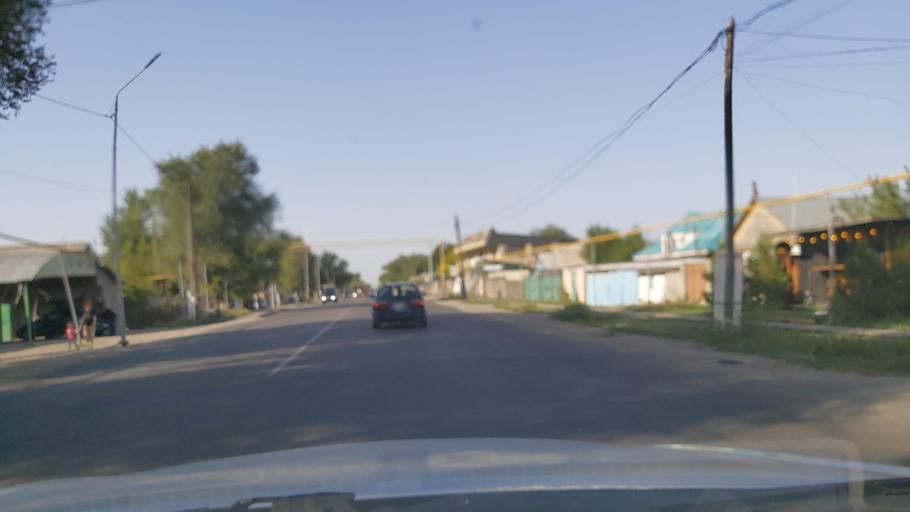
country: KZ
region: Almaty Oblysy
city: Energeticheskiy
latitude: 43.4995
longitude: 77.0415
